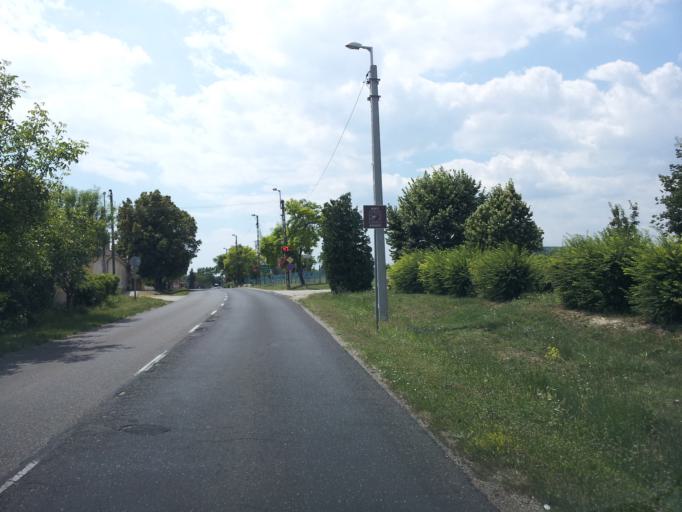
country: HU
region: Somogy
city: Balatonszarszo
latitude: 46.9072
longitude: 17.8079
